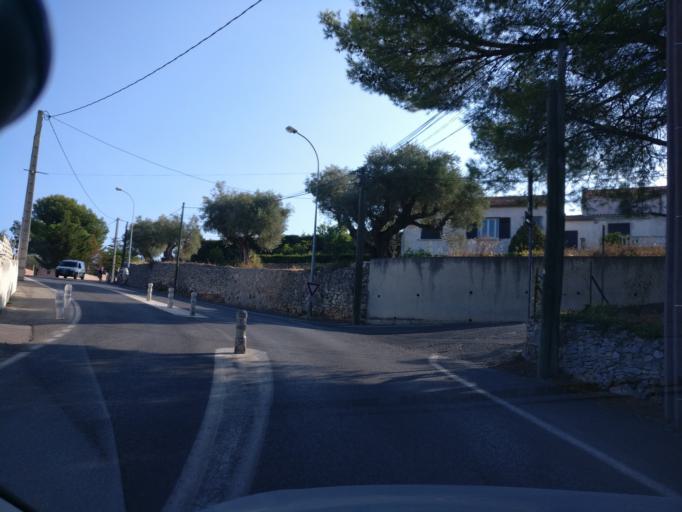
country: FR
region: Provence-Alpes-Cote d'Azur
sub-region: Departement du Var
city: Ollioules
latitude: 43.1342
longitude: 5.8382
